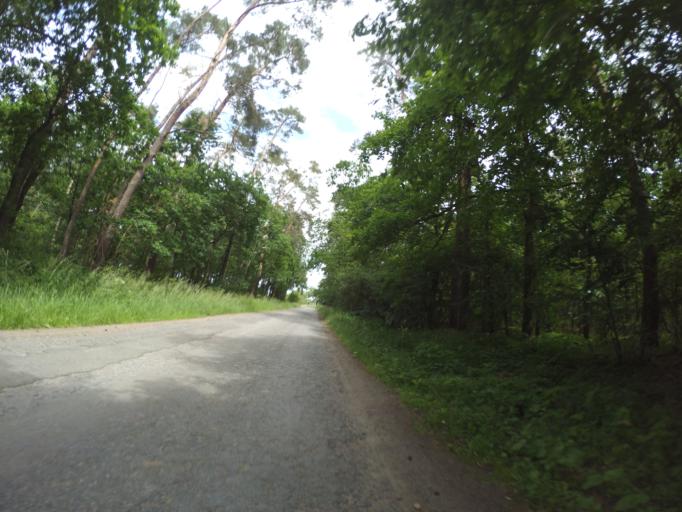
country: CZ
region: Central Bohemia
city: Prerov nad Labem
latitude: 50.1820
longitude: 14.7999
